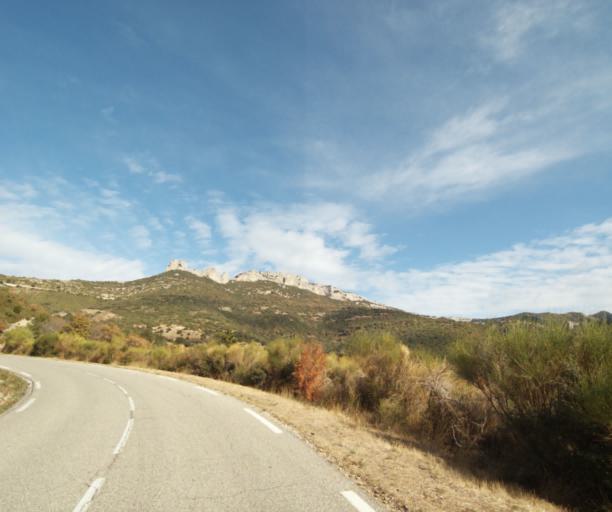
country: FR
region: Provence-Alpes-Cote d'Azur
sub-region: Departement des Bouches-du-Rhone
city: Gemenos
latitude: 43.3083
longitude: 5.6646
